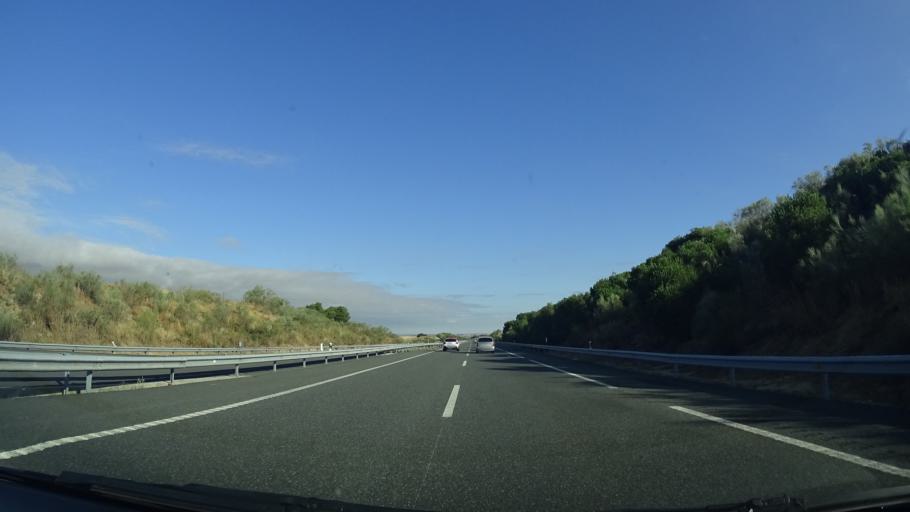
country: ES
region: Castille and Leon
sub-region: Provincia de Segovia
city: Labajos
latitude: 40.8435
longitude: -4.5385
